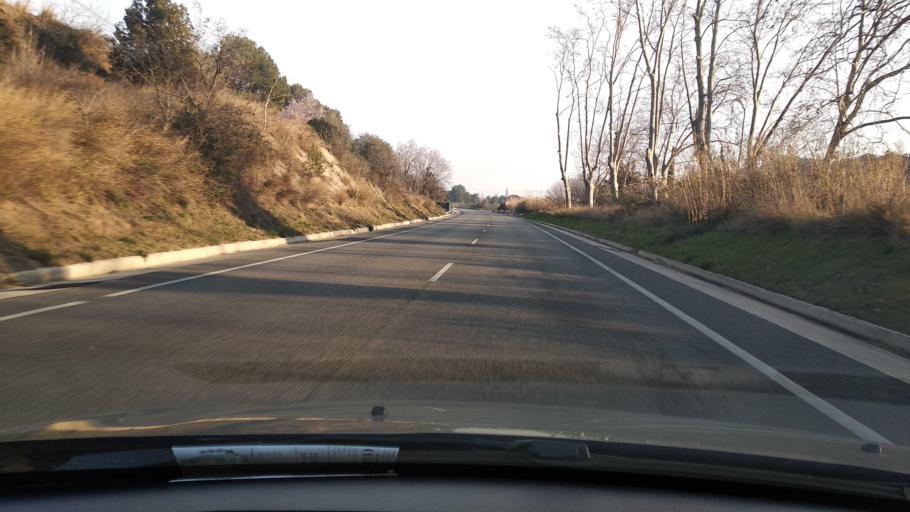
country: ES
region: Catalonia
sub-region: Provincia de Tarragona
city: les Borges del Camp
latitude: 41.1868
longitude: 1.0037
